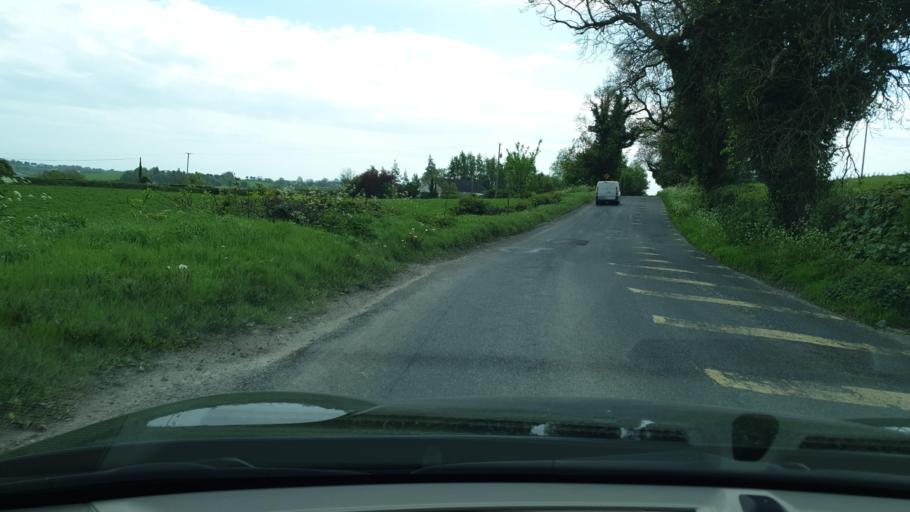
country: IE
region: Ulster
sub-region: An Cabhan
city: Kingscourt
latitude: 53.8306
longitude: -6.7588
